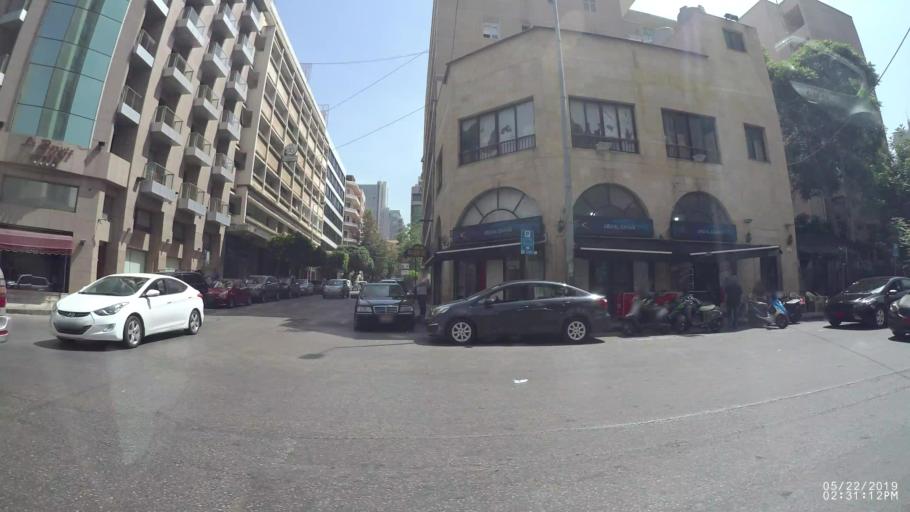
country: LB
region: Beyrouth
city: Ra's Bayrut
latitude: 33.9011
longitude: 35.4927
